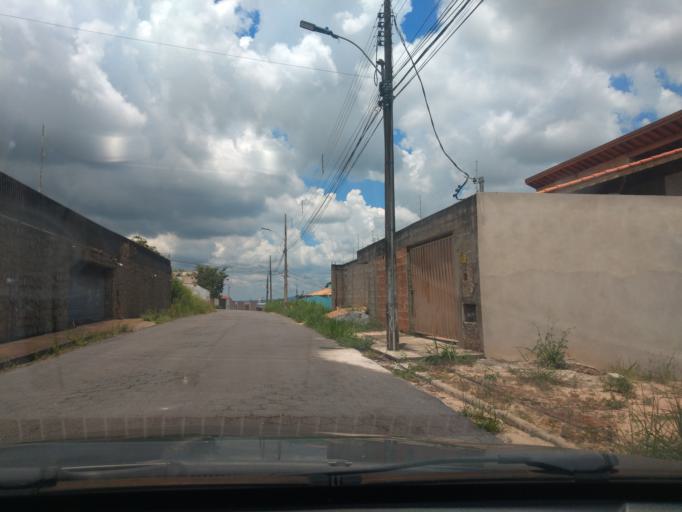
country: BR
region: Minas Gerais
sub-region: Tres Coracoes
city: Tres Coracoes
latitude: -21.6912
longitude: -45.2624
